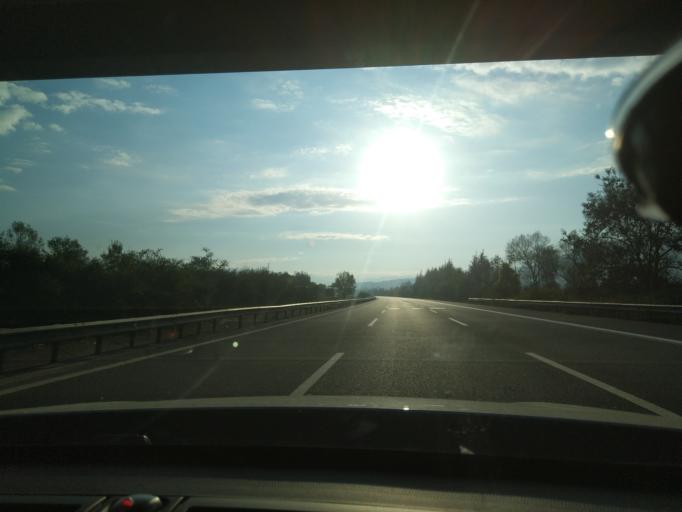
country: TR
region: Duzce
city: Duzce
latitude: 40.7933
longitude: 31.2031
